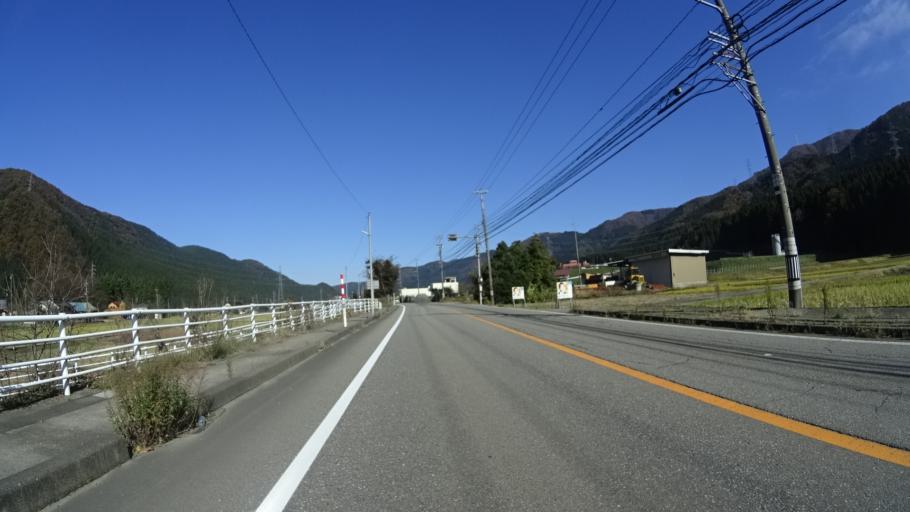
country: JP
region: Ishikawa
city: Tsurugi-asahimachi
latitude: 36.4145
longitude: 136.6321
